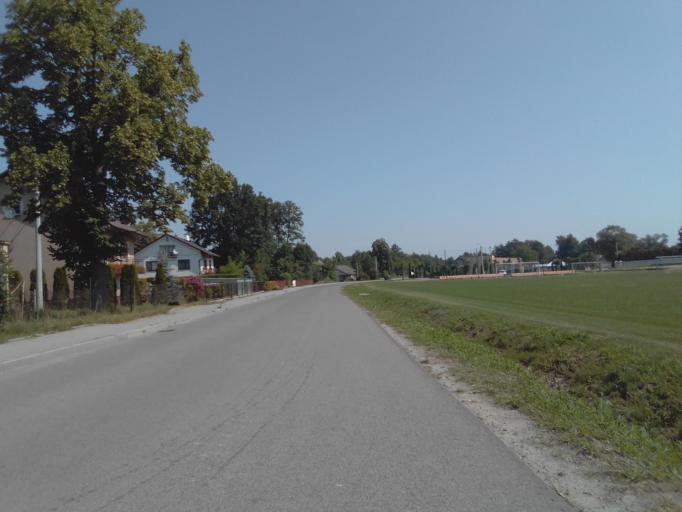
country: PL
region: Subcarpathian Voivodeship
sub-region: Powiat ropczycko-sedziszowski
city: Zagorzyce
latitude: 50.0474
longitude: 21.6629
